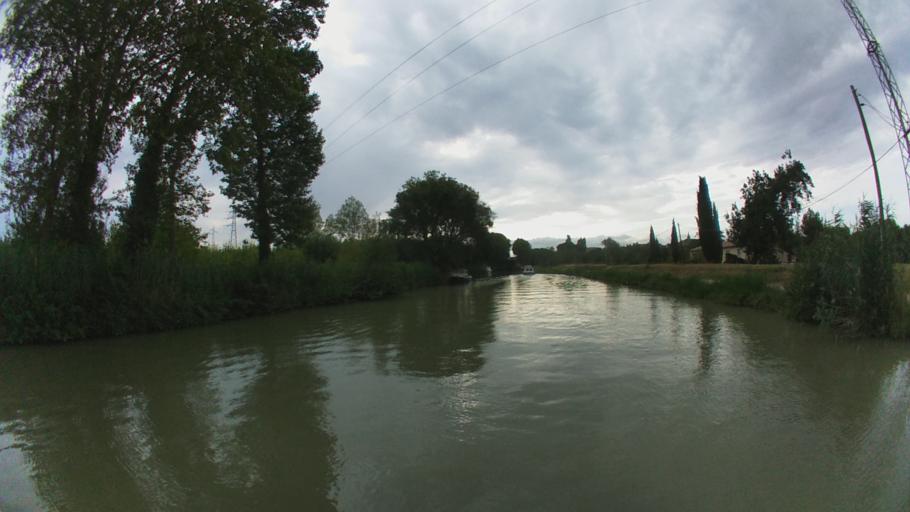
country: FR
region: Languedoc-Roussillon
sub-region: Departement de l'Aude
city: Castelnaudary
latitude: 43.3110
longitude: 1.9651
